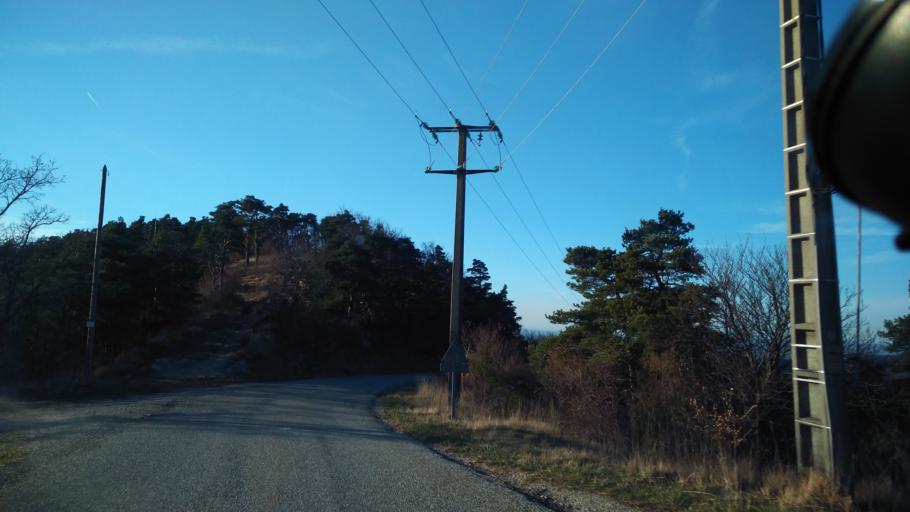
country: FR
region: Rhone-Alpes
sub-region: Departement de la Drome
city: Chabeuil
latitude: 44.8526
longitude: 5.0882
